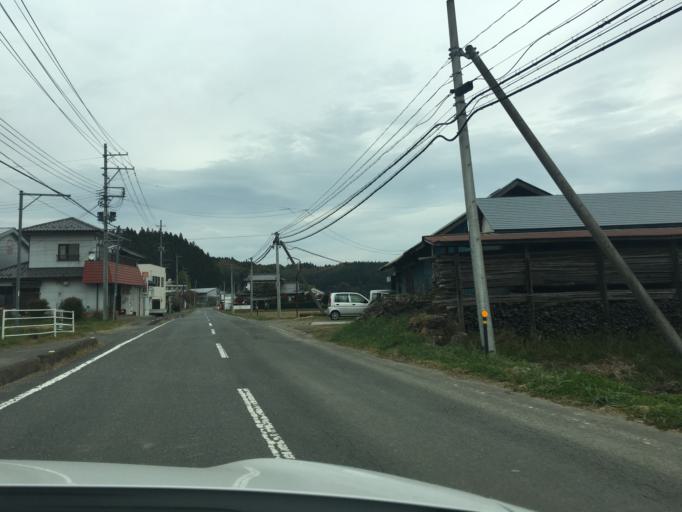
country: JP
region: Fukushima
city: Ishikawa
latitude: 37.1961
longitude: 140.6350
